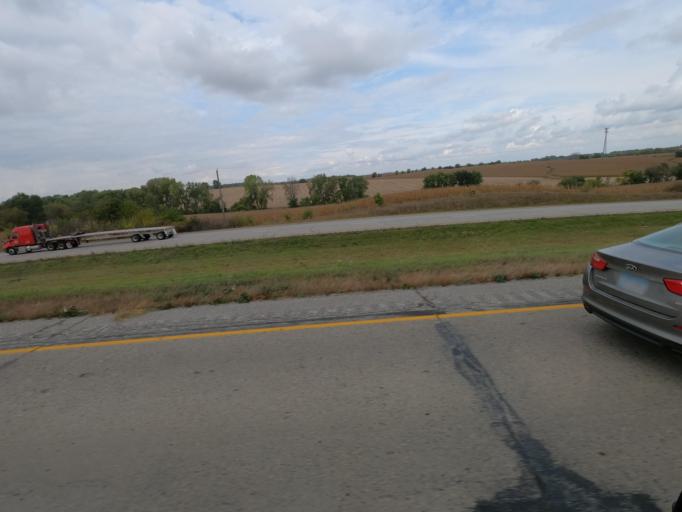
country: US
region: Iowa
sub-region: Polk County
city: Mitchellville
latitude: 41.6005
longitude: -93.3827
